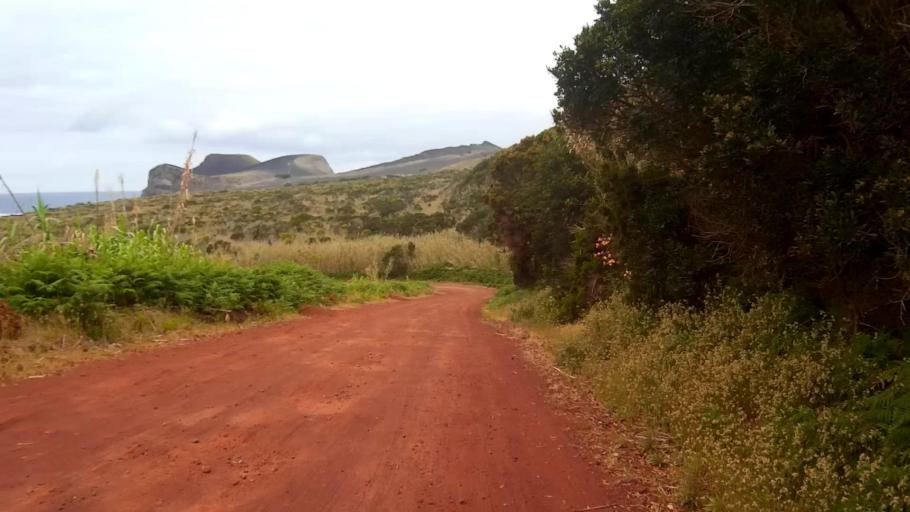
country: PT
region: Azores
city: Ribeira Grande
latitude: 38.5868
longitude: -28.8183
